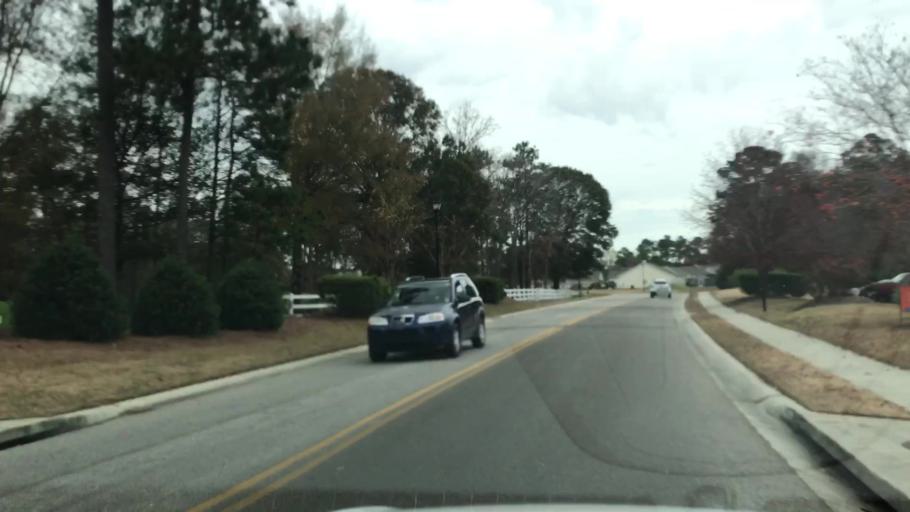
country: US
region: South Carolina
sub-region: Horry County
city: Forestbrook
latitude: 33.7080
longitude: -78.9471
